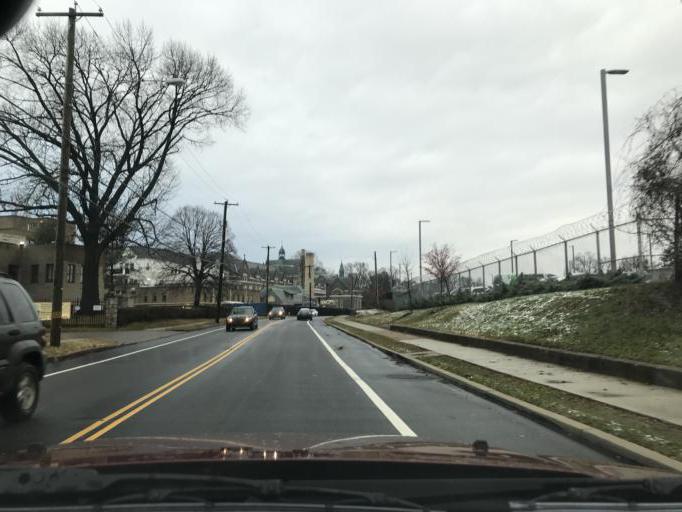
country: US
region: Pennsylvania
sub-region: Montgomery County
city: Bala-Cynwyd
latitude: 39.9977
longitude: -75.2166
